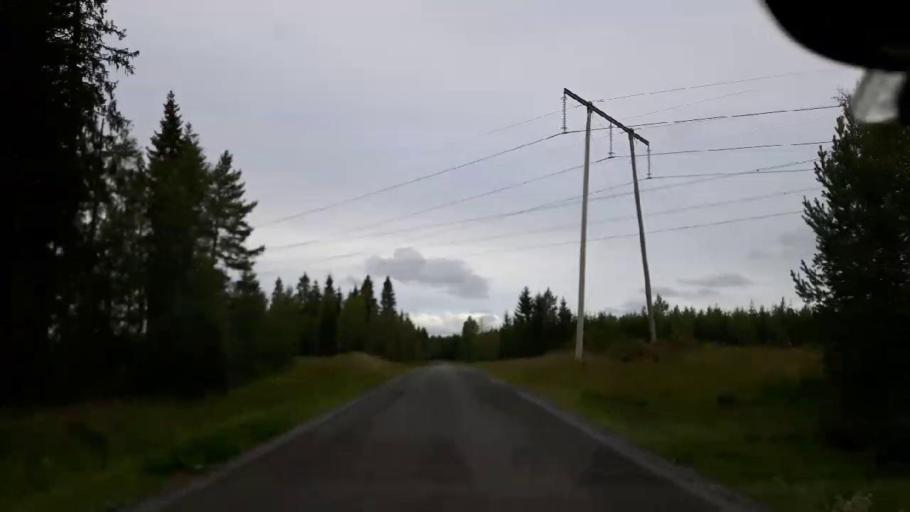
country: SE
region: Jaemtland
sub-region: Krokoms Kommun
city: Krokom
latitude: 63.3166
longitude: 14.3134
